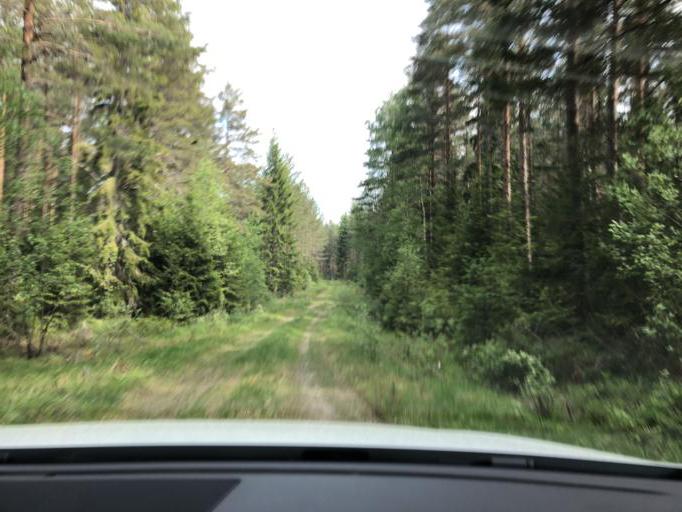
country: SE
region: Dalarna
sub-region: Avesta Kommun
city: Horndal
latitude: 60.2180
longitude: 16.5043
